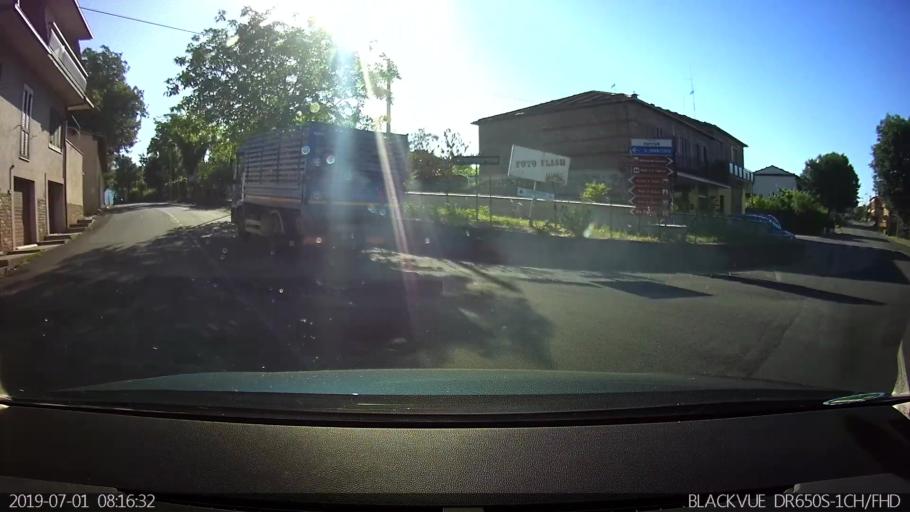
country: IT
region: Latium
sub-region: Provincia di Frosinone
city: Veroli
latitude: 41.7006
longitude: 13.4333
